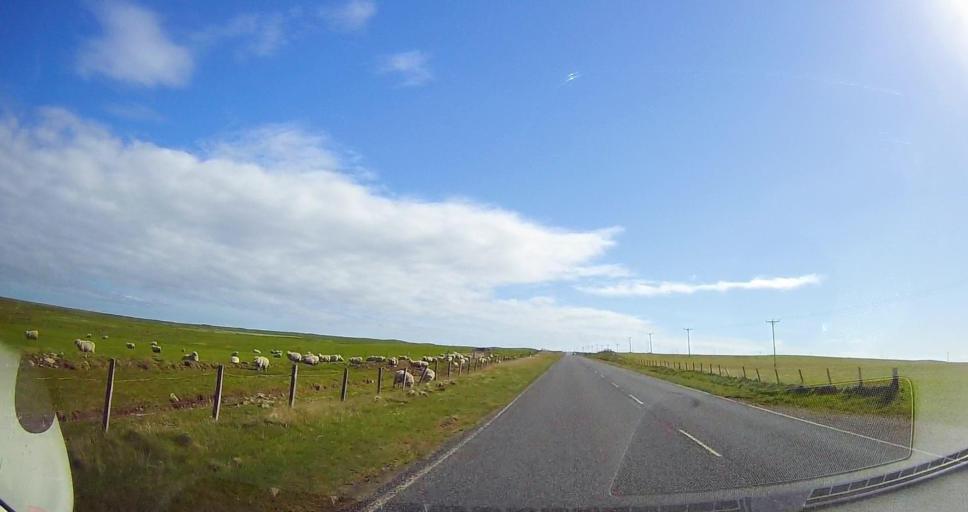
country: GB
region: Scotland
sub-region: Shetland Islands
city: Sandwick
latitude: 59.9067
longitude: -1.3021
